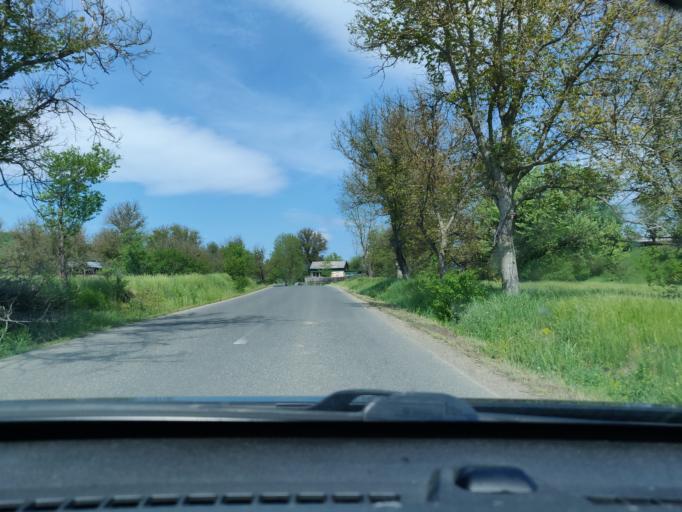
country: RO
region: Vrancea
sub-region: Comuna Vidra
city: Vidra
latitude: 45.9474
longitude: 26.8688
